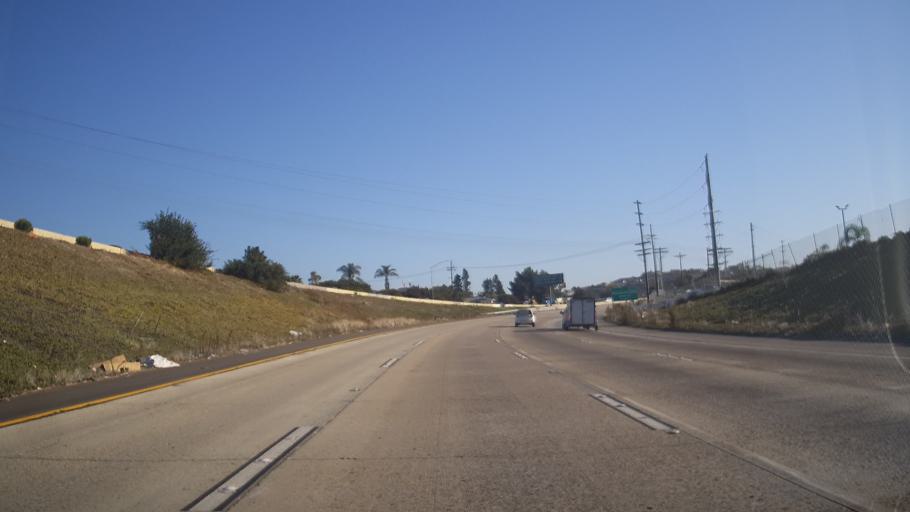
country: US
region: California
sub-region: San Diego County
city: Lemon Grove
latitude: 32.7446
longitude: -117.0451
